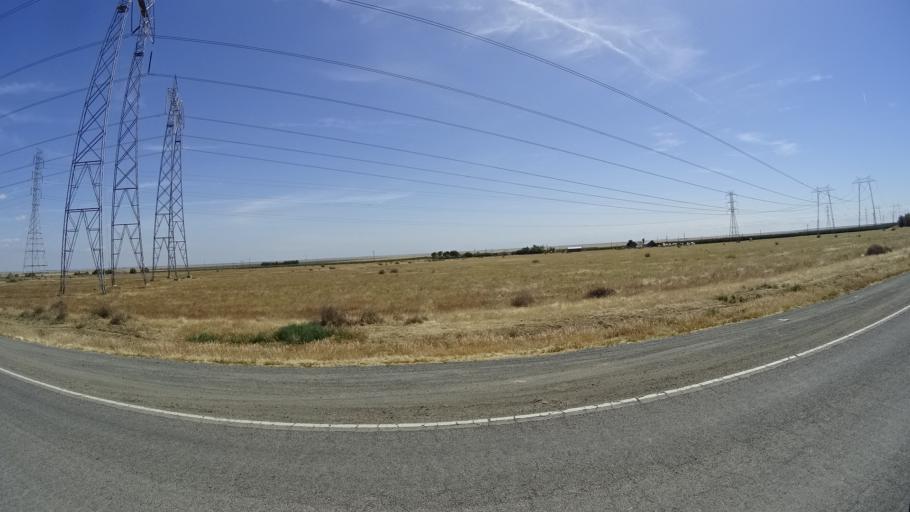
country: US
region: California
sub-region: Kings County
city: Kettleman City
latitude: 35.9947
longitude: -119.9565
